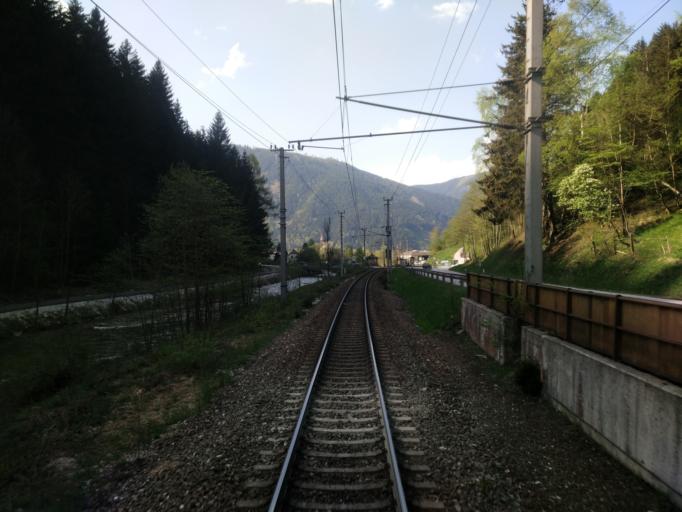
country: AT
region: Styria
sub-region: Politischer Bezirk Liezen
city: Selzthal
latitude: 47.5419
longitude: 14.3073
